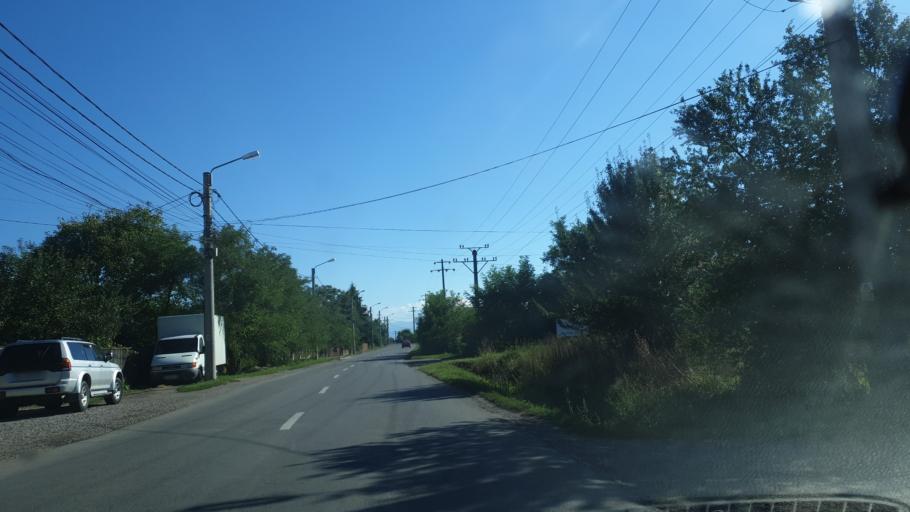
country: RO
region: Covasna
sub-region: Municipiul Sfantu Gheorghe
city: Sfantu-Gheorghe
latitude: 45.8479
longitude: 25.7775
